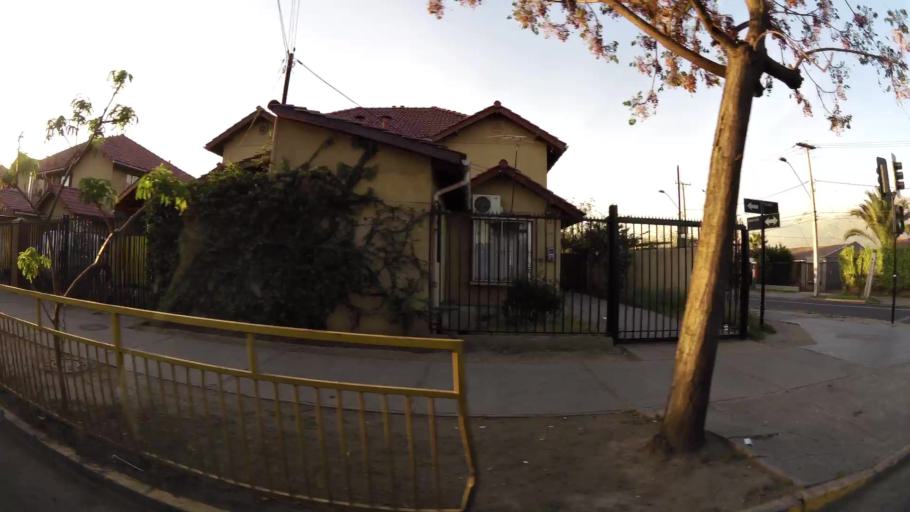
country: CL
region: Santiago Metropolitan
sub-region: Provincia de Cordillera
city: Puente Alto
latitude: -33.5975
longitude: -70.5726
